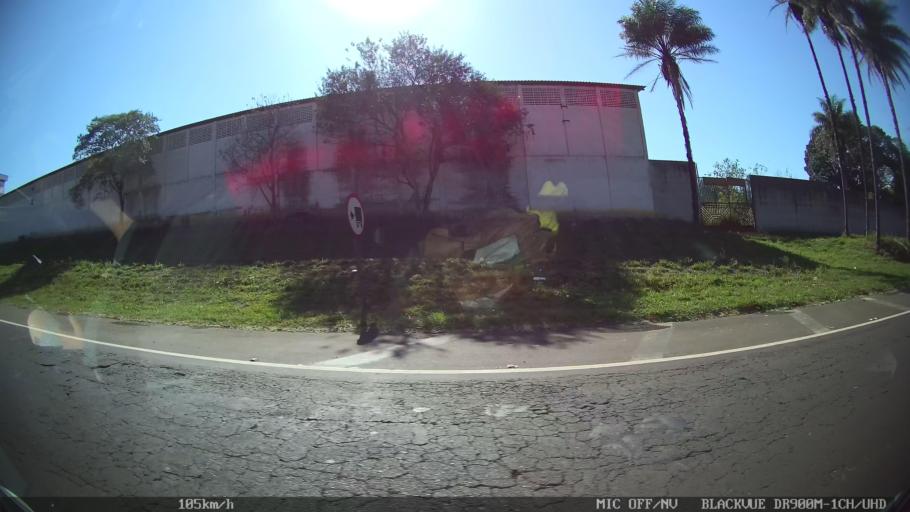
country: BR
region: Sao Paulo
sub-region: Batatais
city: Batatais
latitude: -20.9101
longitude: -47.5921
